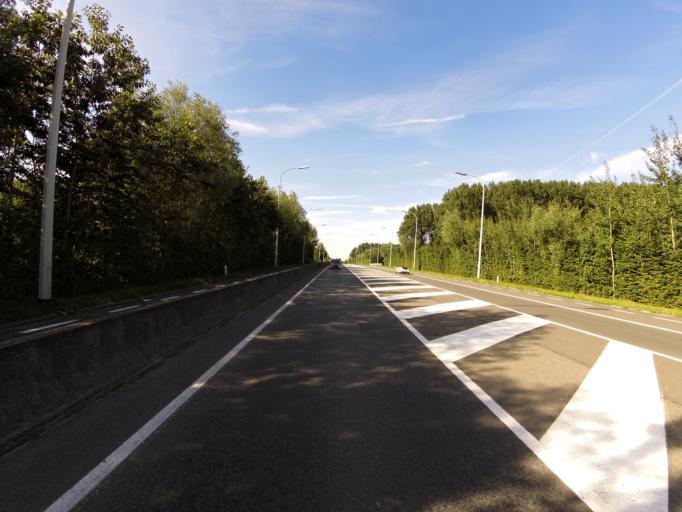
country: BE
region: Flanders
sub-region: Provincie Oost-Vlaanderen
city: Maldegem
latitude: 51.2319
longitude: 3.4468
